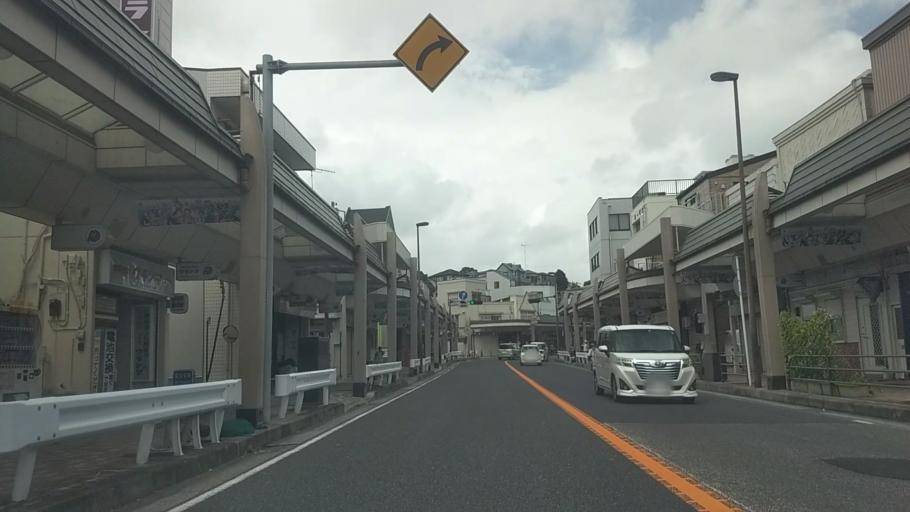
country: JP
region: Kanagawa
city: Yokosuka
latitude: 35.2722
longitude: 139.6710
